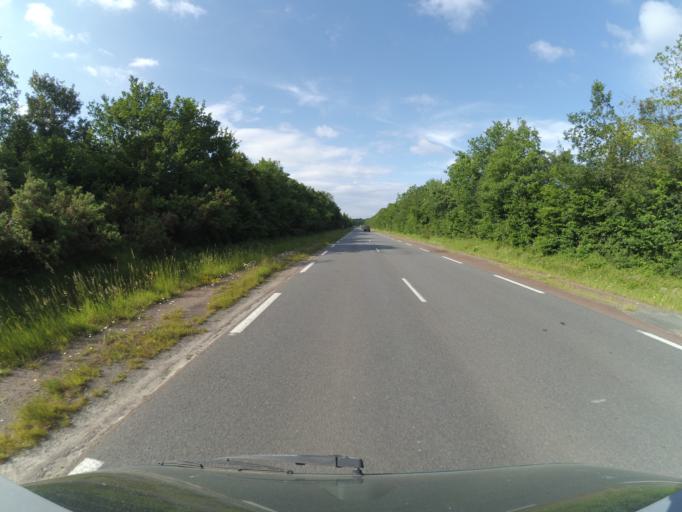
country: FR
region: Poitou-Charentes
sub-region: Departement de la Charente-Maritime
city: Saint-Agnant
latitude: 45.8093
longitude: -0.9335
